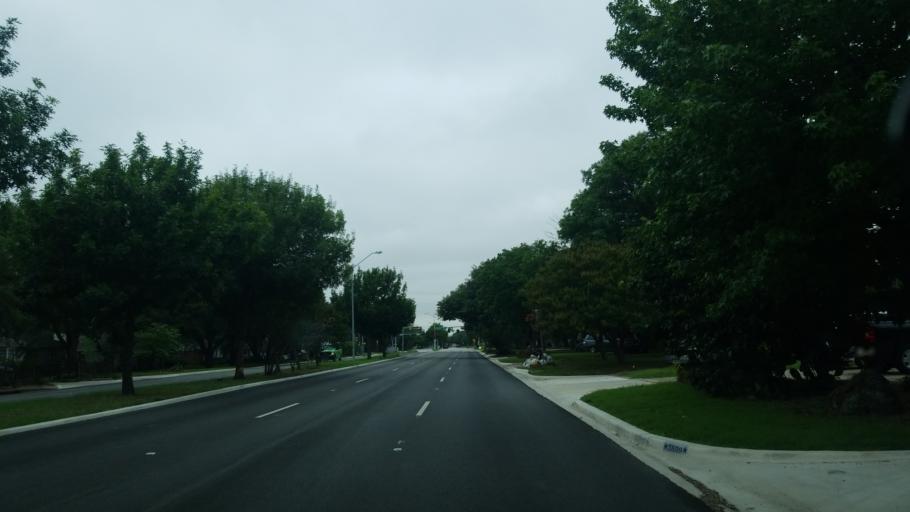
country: US
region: Texas
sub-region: Dallas County
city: Farmers Branch
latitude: 32.8952
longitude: -96.8605
